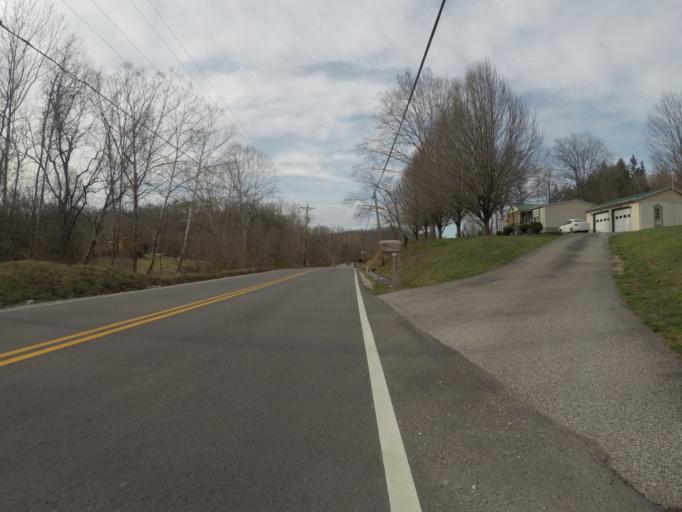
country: US
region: Ohio
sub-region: Lawrence County
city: Burlington
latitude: 38.4413
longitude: -82.5006
